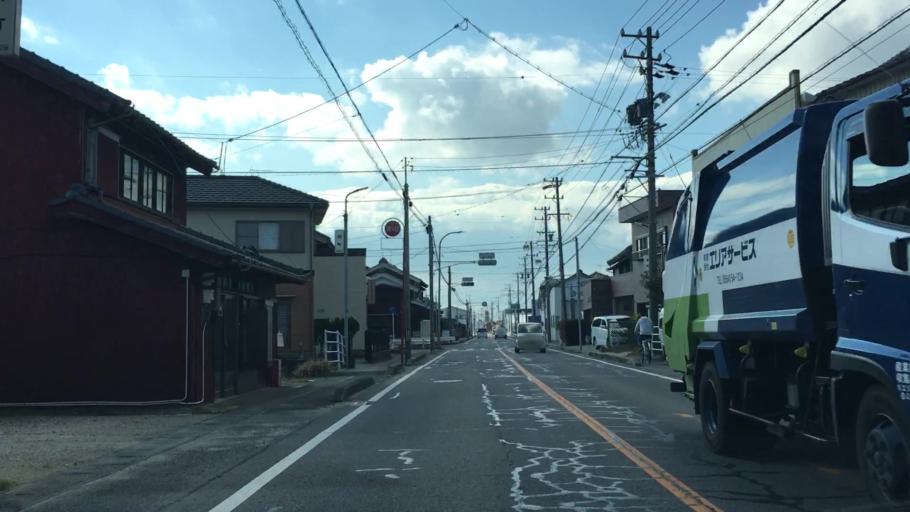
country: JP
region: Aichi
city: Ishiki
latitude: 34.7957
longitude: 137.0640
